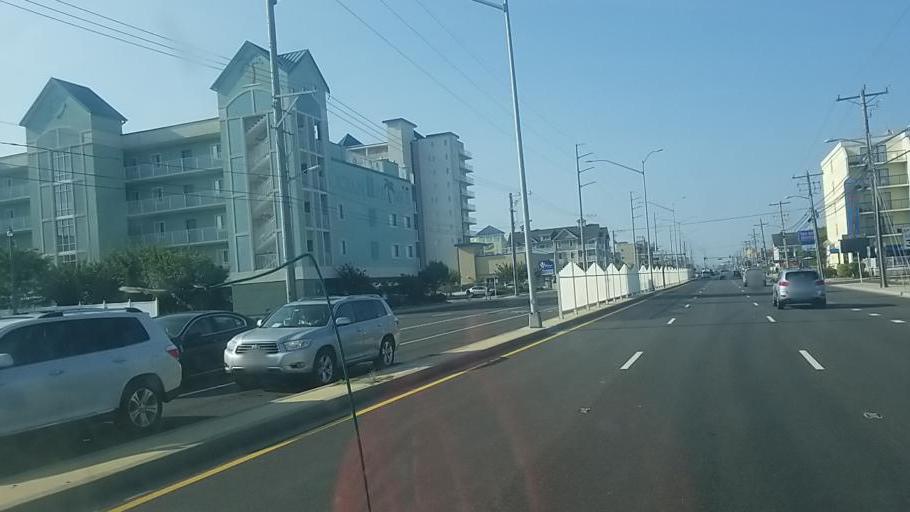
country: US
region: Maryland
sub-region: Worcester County
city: Ocean City
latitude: 38.3849
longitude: -75.0665
